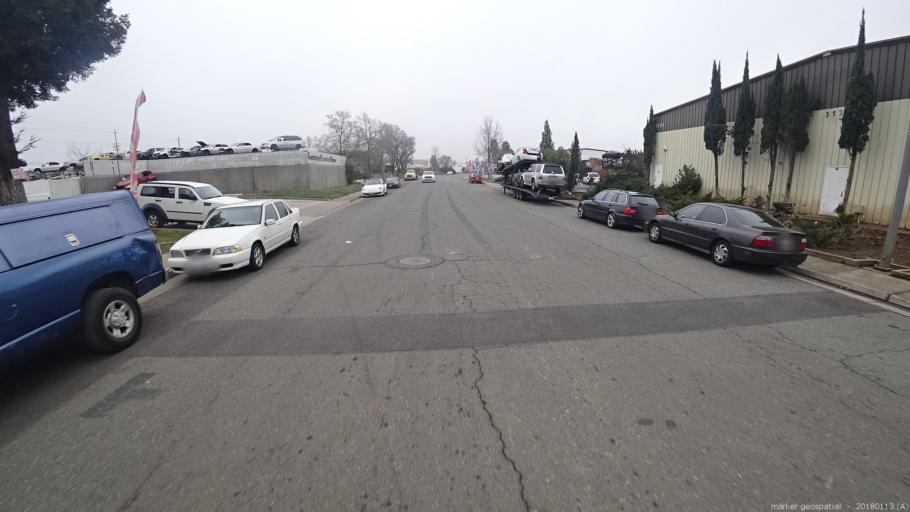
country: US
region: California
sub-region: Sacramento County
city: Rancho Cordova
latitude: 38.5686
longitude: -121.2539
